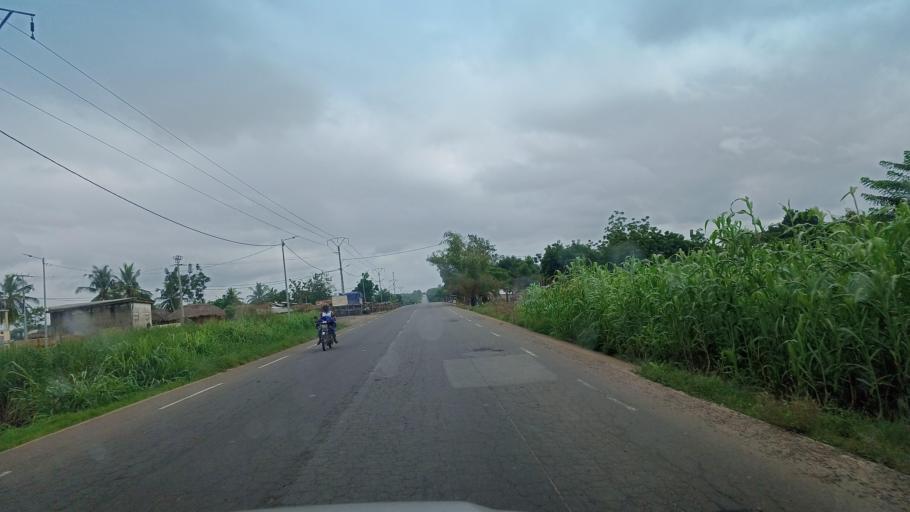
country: TG
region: Maritime
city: Tsevie
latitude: 6.5542
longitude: 1.1846
